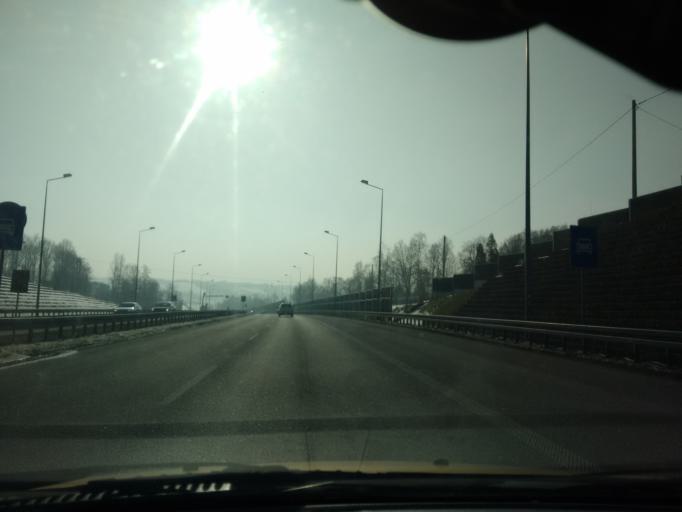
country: PL
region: Silesian Voivodeship
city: Janowice
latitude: 49.8404
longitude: 19.0888
